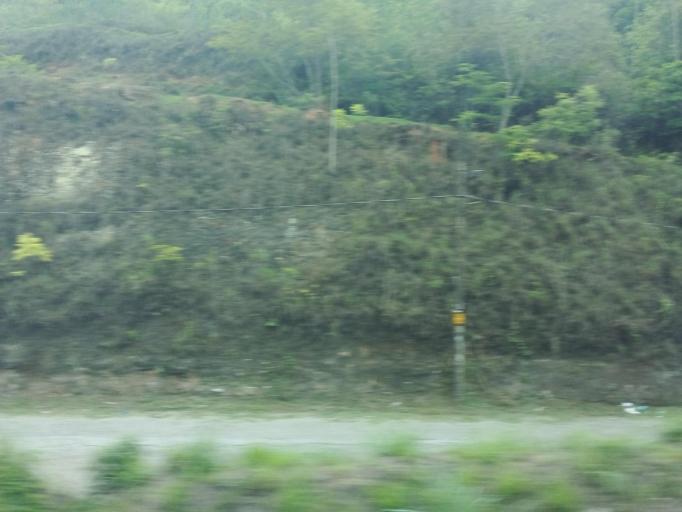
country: BR
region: Minas Gerais
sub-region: Joao Monlevade
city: Joao Monlevade
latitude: -19.8480
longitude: -43.1230
